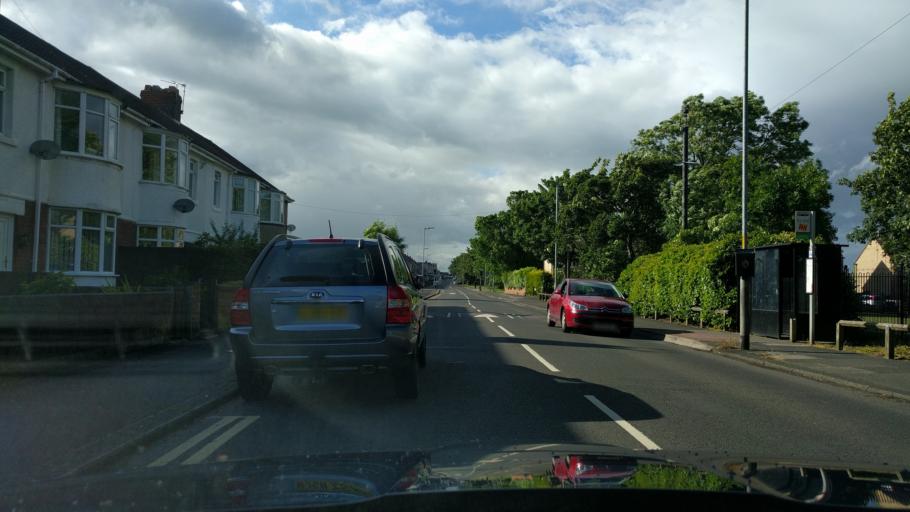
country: GB
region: England
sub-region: Northumberland
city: Lynemouth
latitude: 55.1815
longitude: -1.5559
